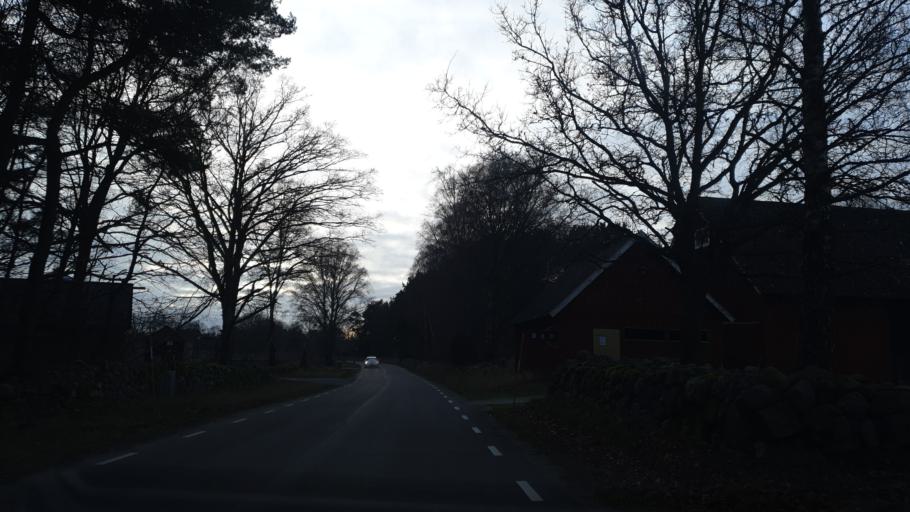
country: SE
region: Kalmar
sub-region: Torsas Kommun
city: Torsas
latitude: 56.2309
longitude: 15.9961
